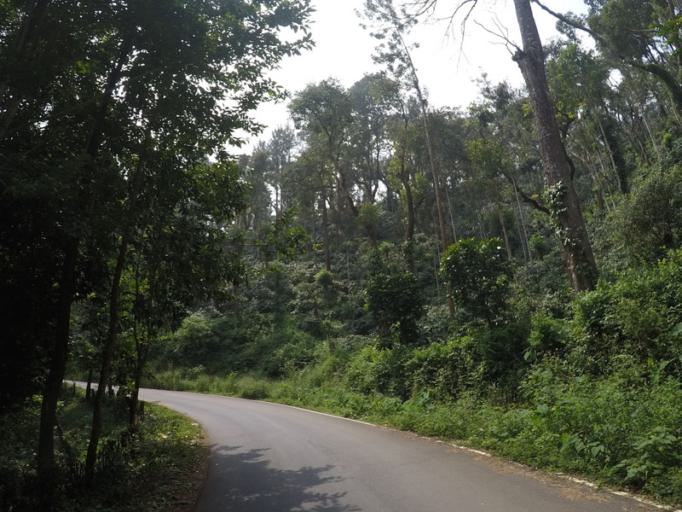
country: IN
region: Karnataka
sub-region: Chikmagalur
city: Mudigere
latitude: 13.1810
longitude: 75.4245
